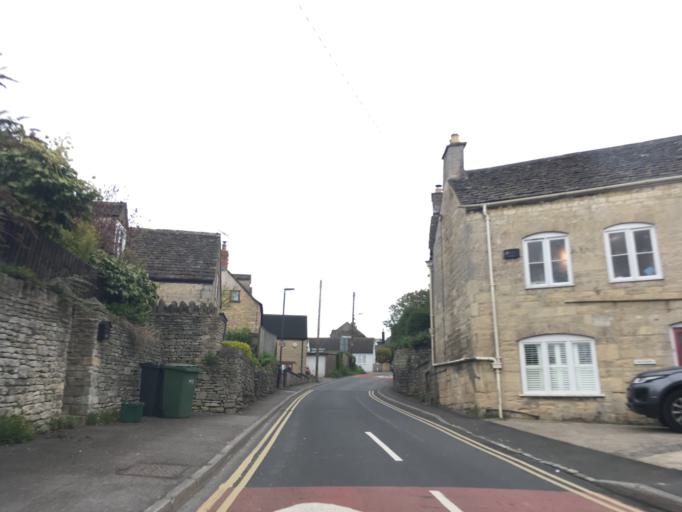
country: GB
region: England
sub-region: Gloucestershire
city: Stroud
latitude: 51.7388
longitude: -2.2247
